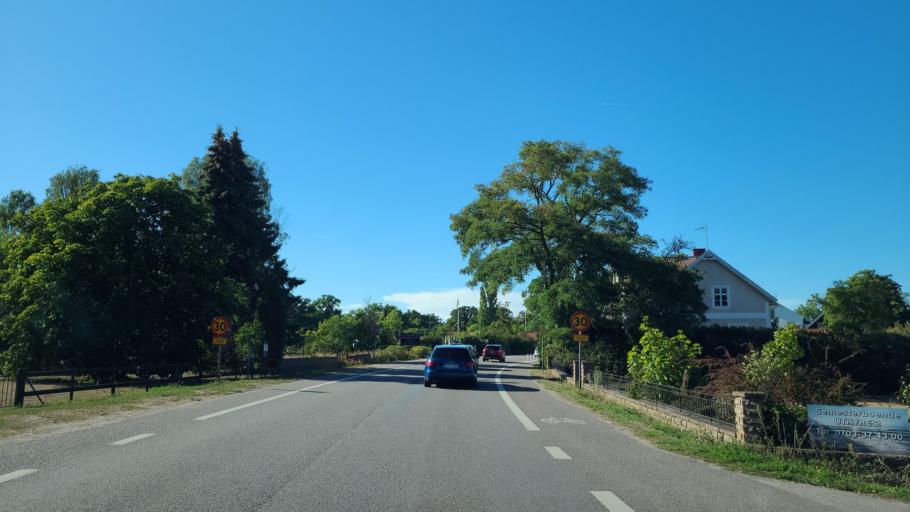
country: SE
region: Kalmar
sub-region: Borgholms Kommun
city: Borgholm
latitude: 57.2455
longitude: 17.0592
